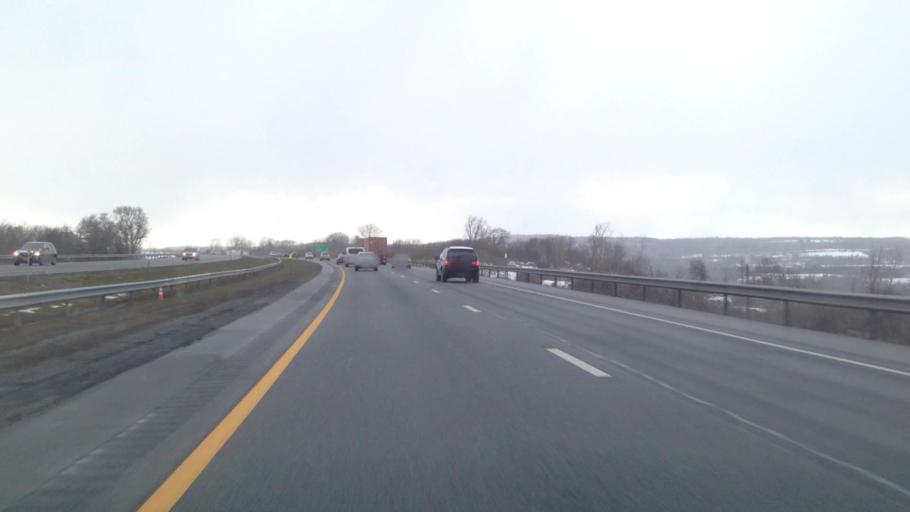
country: US
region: New York
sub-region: Montgomery County
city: Fort Plain
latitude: 42.9561
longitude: -74.6344
